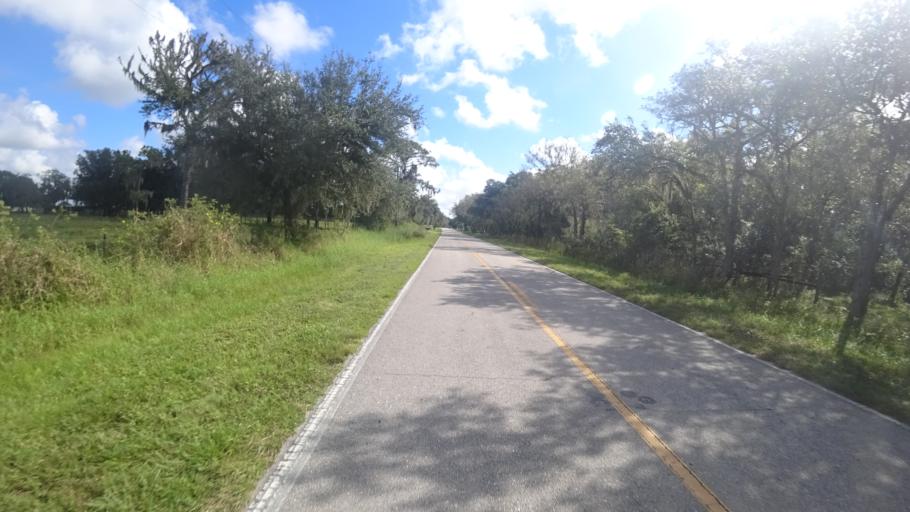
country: US
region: Florida
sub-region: Sarasota County
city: Lake Sarasota
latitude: 27.3444
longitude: -82.2218
